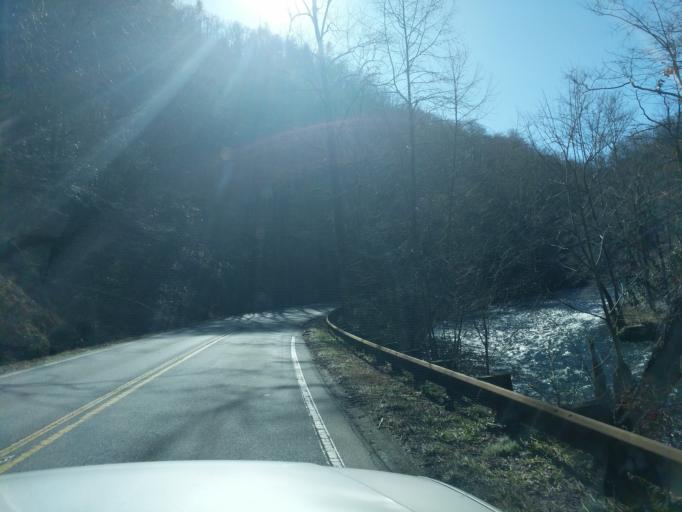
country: US
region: North Carolina
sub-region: Graham County
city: Robbinsville
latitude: 35.3304
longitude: -83.6276
